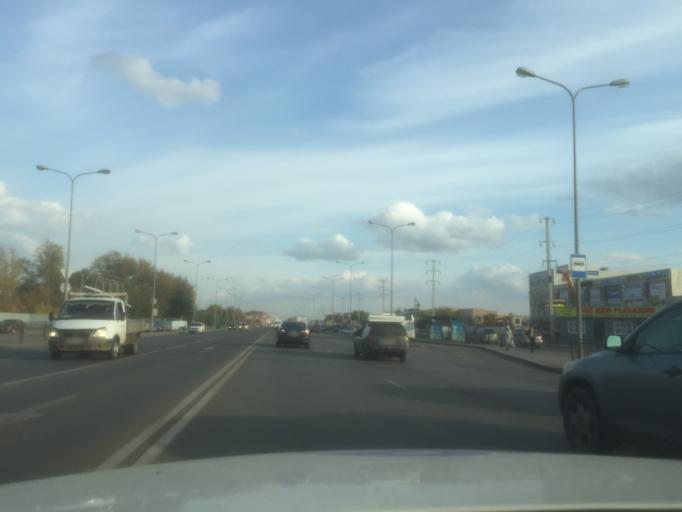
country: KZ
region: Astana Qalasy
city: Astana
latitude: 51.1802
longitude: 71.4640
